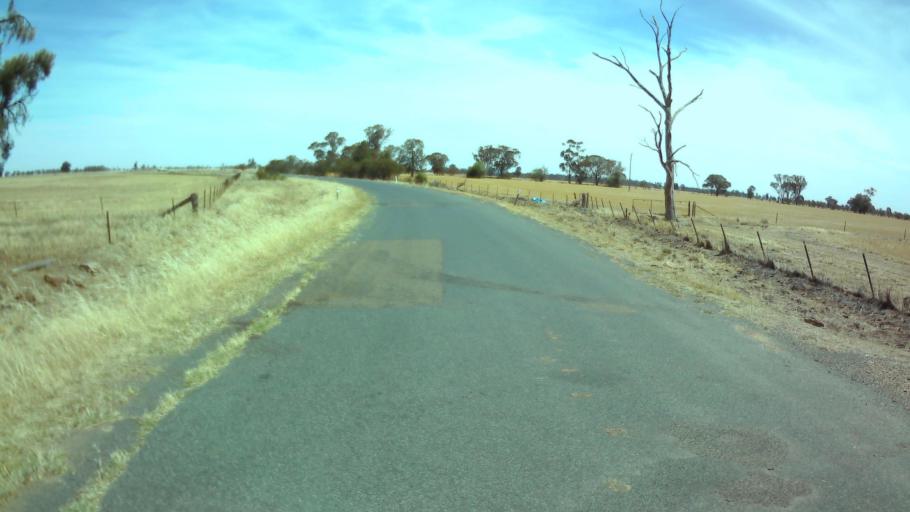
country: AU
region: New South Wales
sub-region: Weddin
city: Grenfell
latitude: -33.9360
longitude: 147.7614
